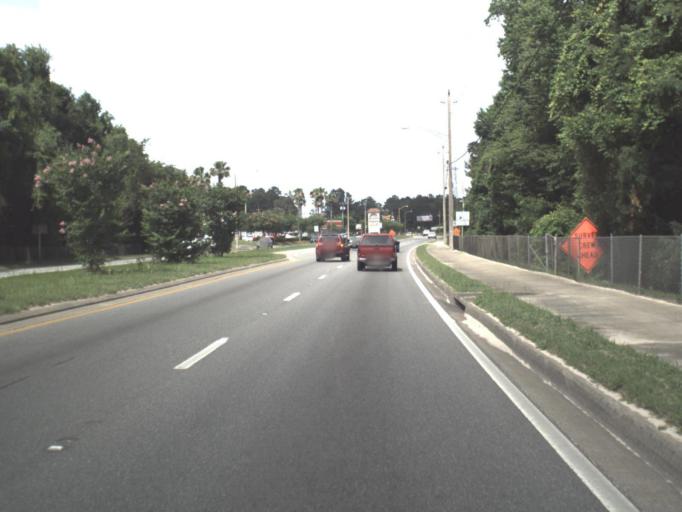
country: US
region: Florida
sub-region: Clay County
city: Middleburg
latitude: 30.0629
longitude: -81.8737
